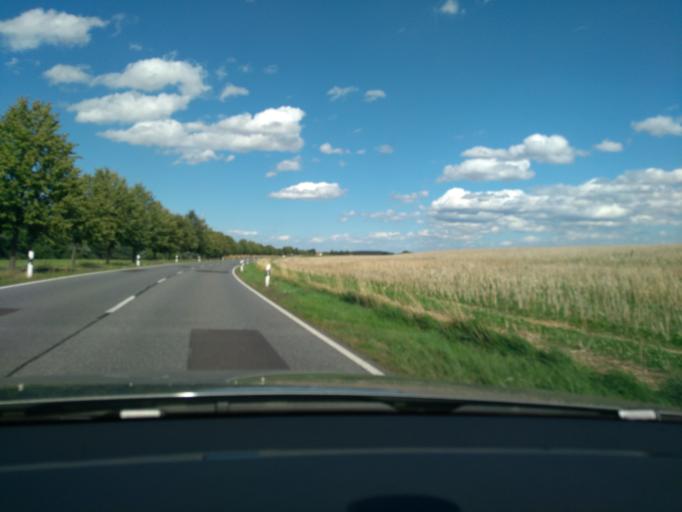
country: DE
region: Saxony
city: Demitz-Thumitz
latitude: 51.1553
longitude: 14.2529
